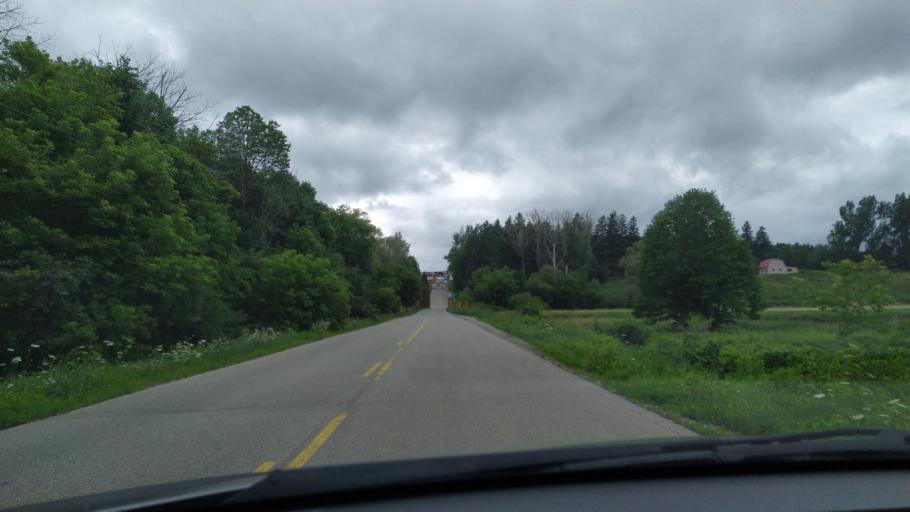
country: CA
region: Ontario
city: Kitchener
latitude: 43.3331
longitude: -80.6419
